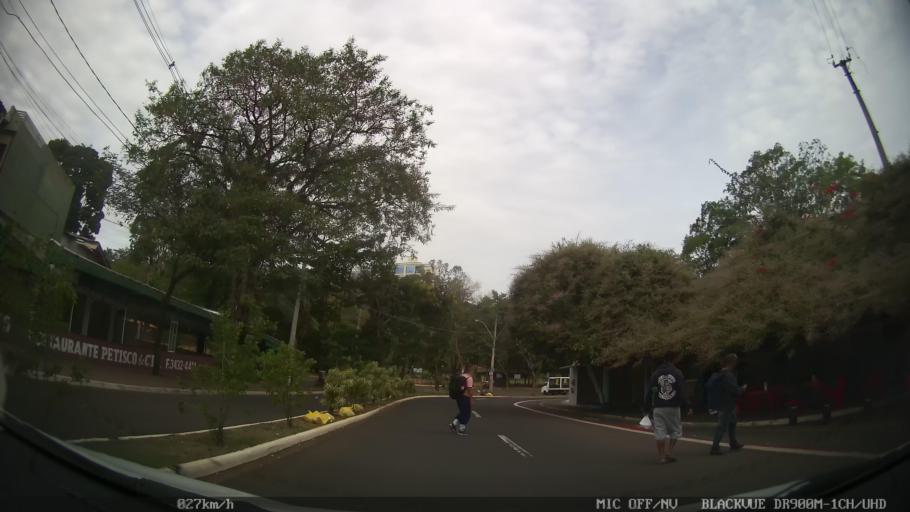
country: BR
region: Sao Paulo
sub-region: Piracicaba
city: Piracicaba
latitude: -22.7248
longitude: -47.6577
